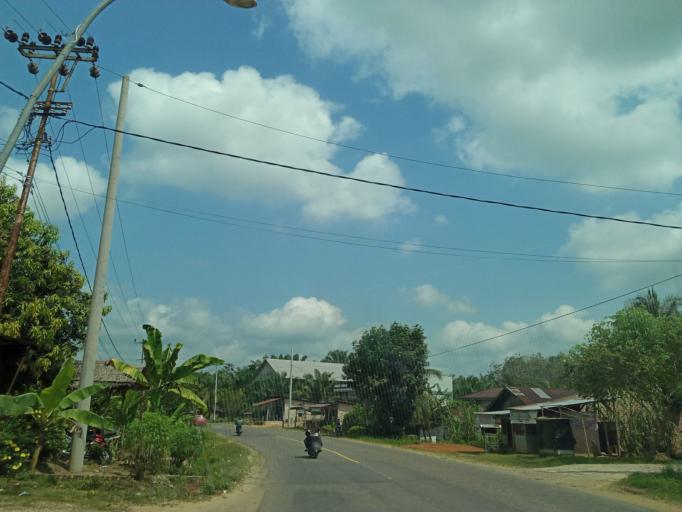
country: ID
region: Jambi
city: Muara Tembesi
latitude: -1.7186
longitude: 103.1262
